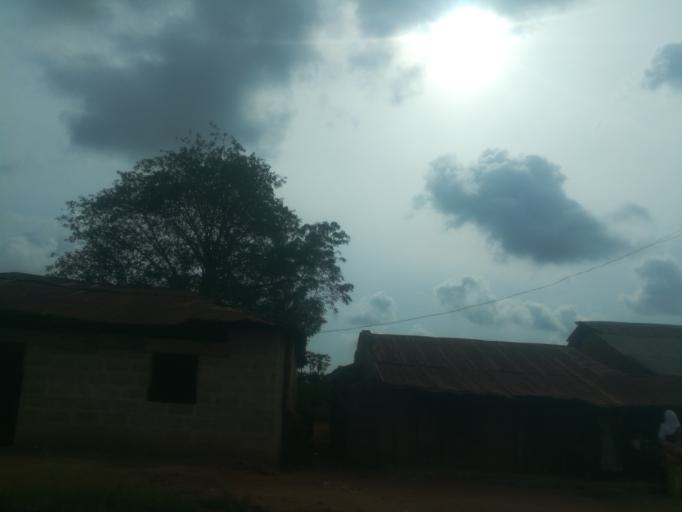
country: NG
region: Ogun
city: Ayetoro
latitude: 7.3927
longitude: 3.0131
